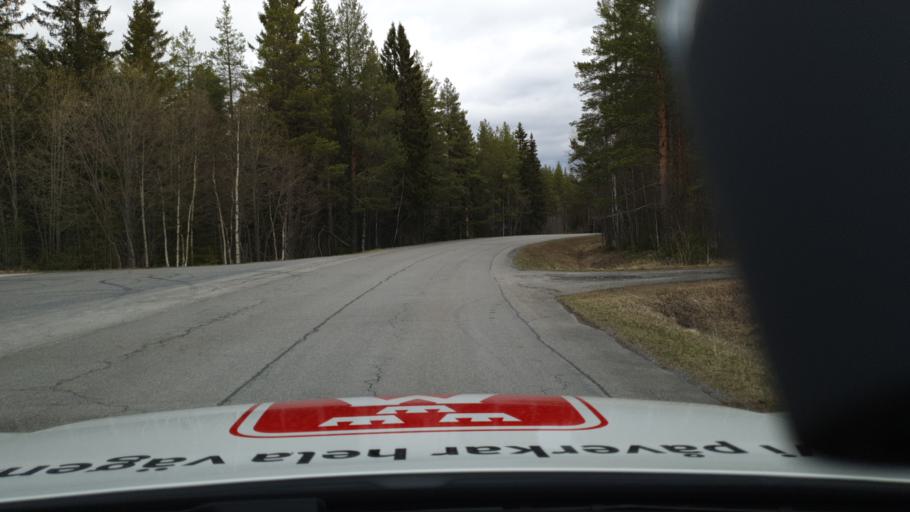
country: SE
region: Jaemtland
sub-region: Krokoms Kommun
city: Krokom
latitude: 63.2046
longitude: 14.4675
